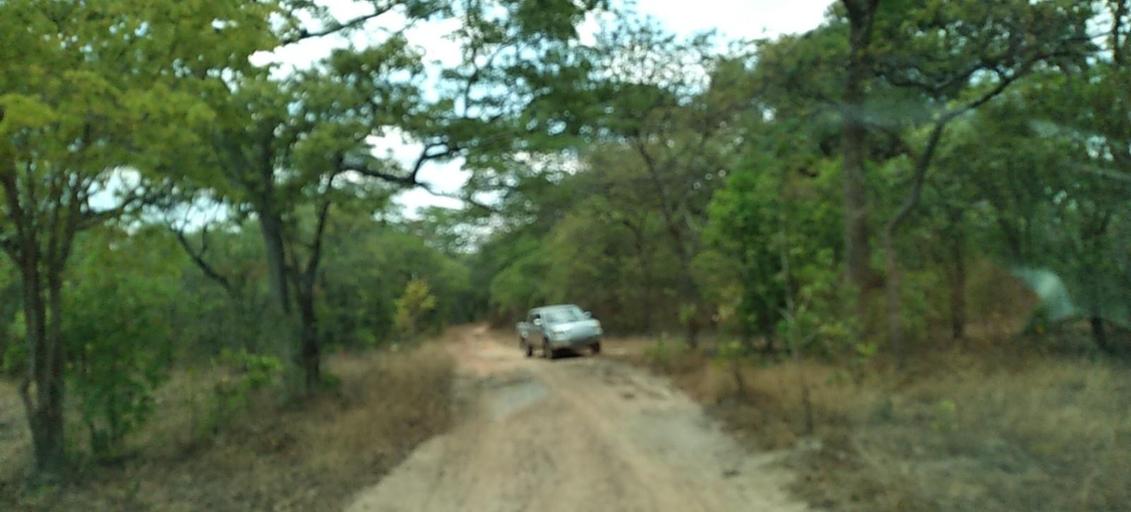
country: ZM
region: Copperbelt
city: Chililabombwe
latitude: -12.4747
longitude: 27.7006
